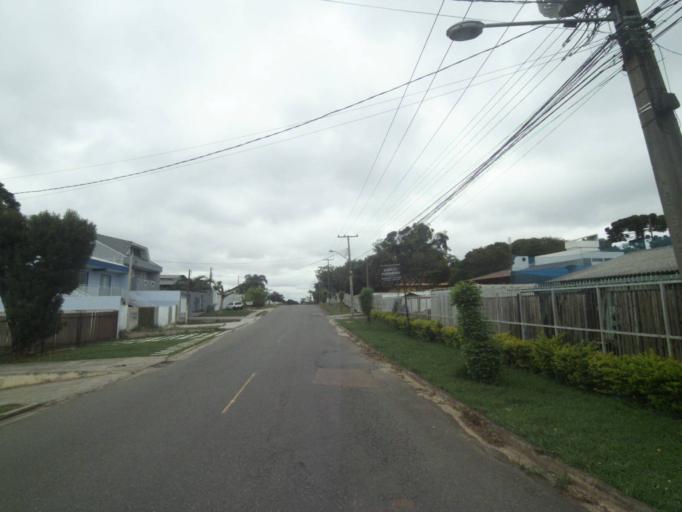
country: BR
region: Parana
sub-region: Sao Jose Dos Pinhais
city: Sao Jose dos Pinhais
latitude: -25.5439
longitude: -49.2928
